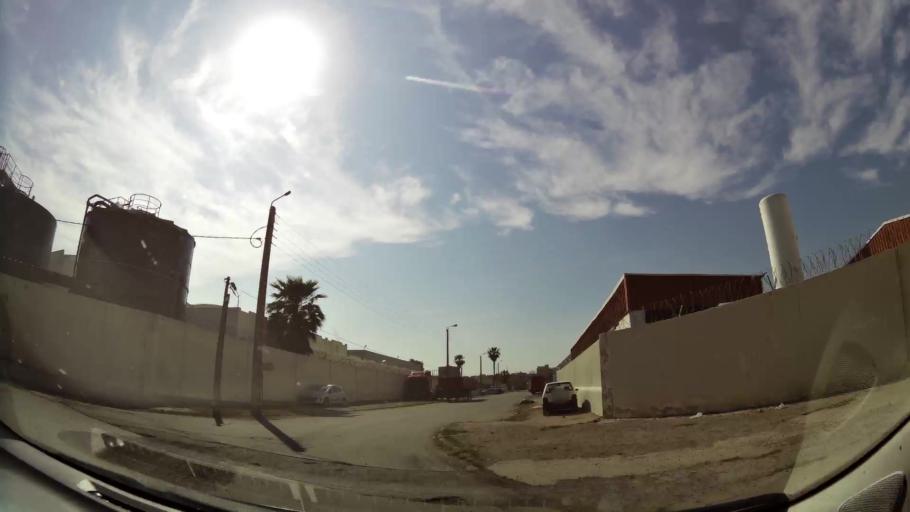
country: MA
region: Oriental
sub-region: Oujda-Angad
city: Oujda
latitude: 34.7044
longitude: -1.8904
